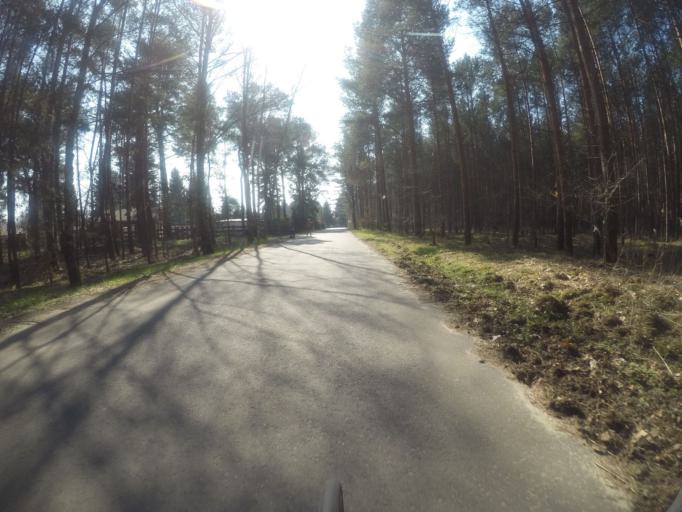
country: DE
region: Berlin
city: Muggelheim
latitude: 52.3784
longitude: 13.6975
